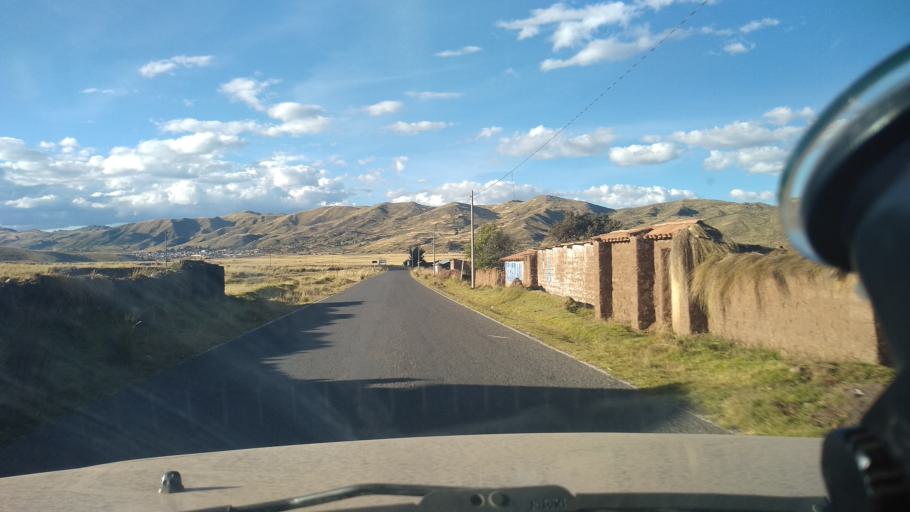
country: PE
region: Cusco
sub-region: Provincia de Canas
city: Chignayhua
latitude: -14.2518
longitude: -71.4369
